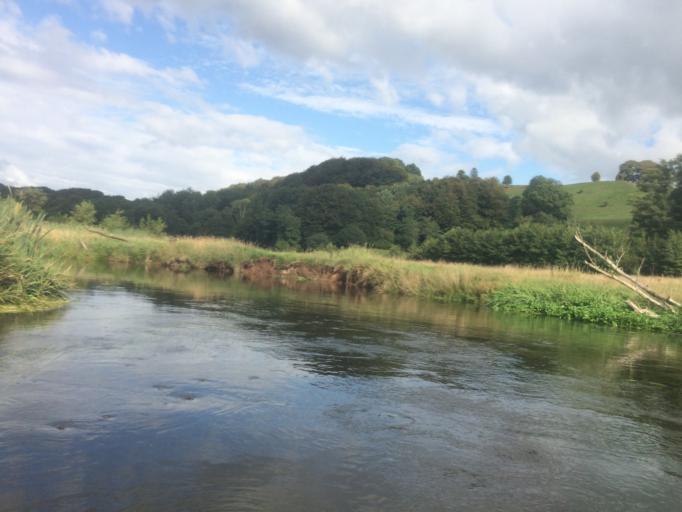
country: DK
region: South Denmark
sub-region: Vejle Kommune
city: Egtved
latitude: 55.6548
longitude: 9.3125
